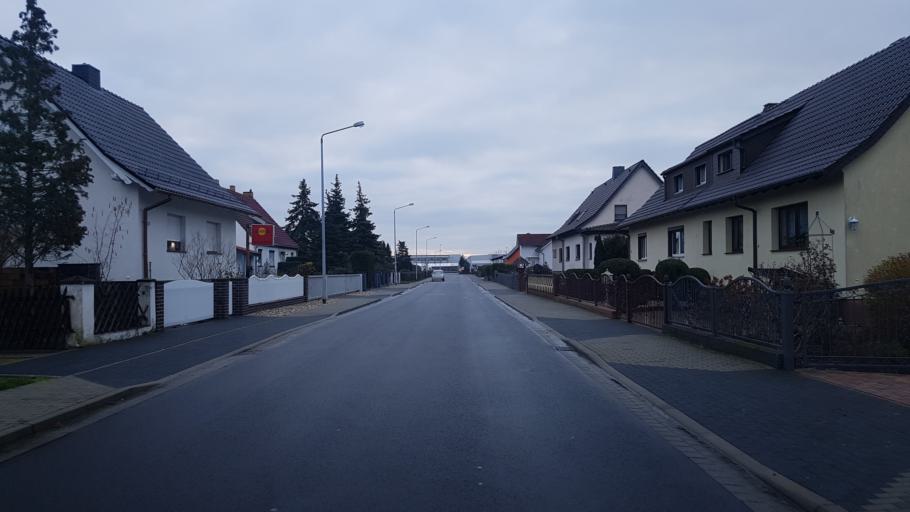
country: DE
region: Brandenburg
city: Elsterwerda
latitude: 51.4619
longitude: 13.5344
